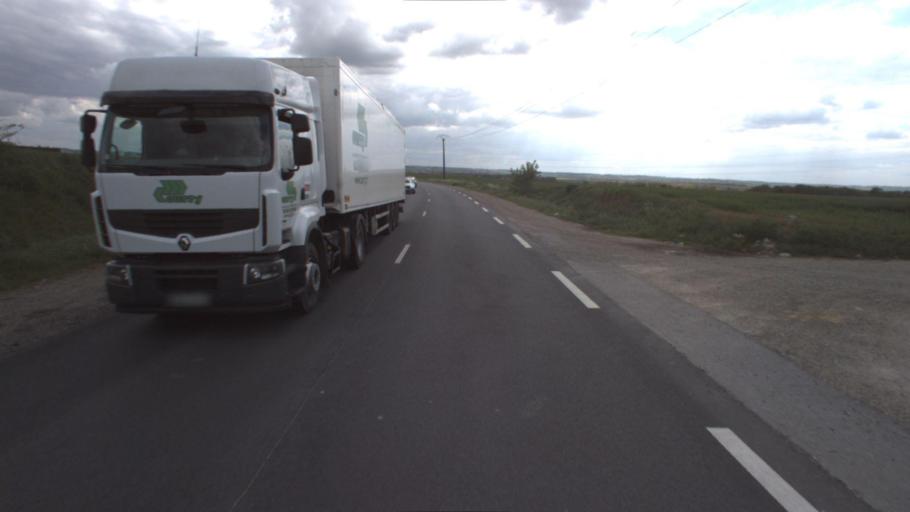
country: FR
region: Ile-de-France
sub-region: Departement de Seine-et-Marne
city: Chauconin-Neufmontiers
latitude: 48.9719
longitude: 2.8568
